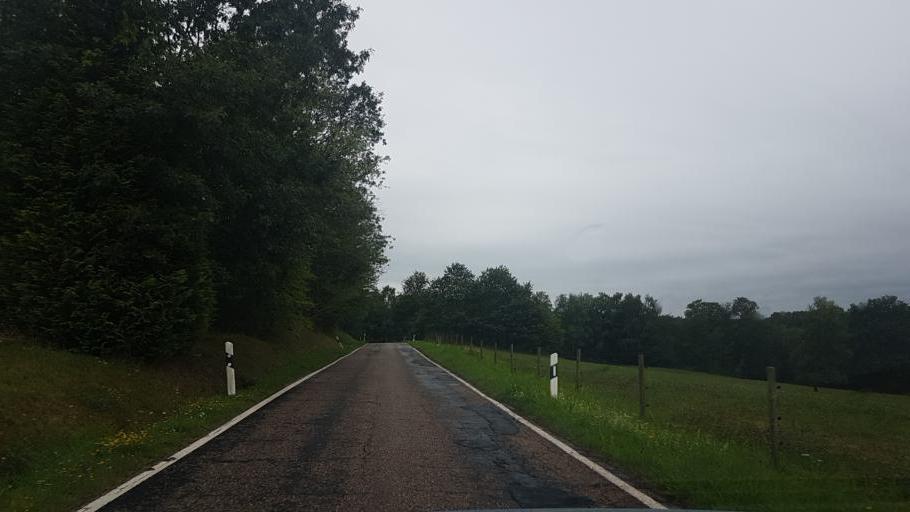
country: DE
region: Saarland
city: Wadern
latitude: 49.5569
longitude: 6.9244
